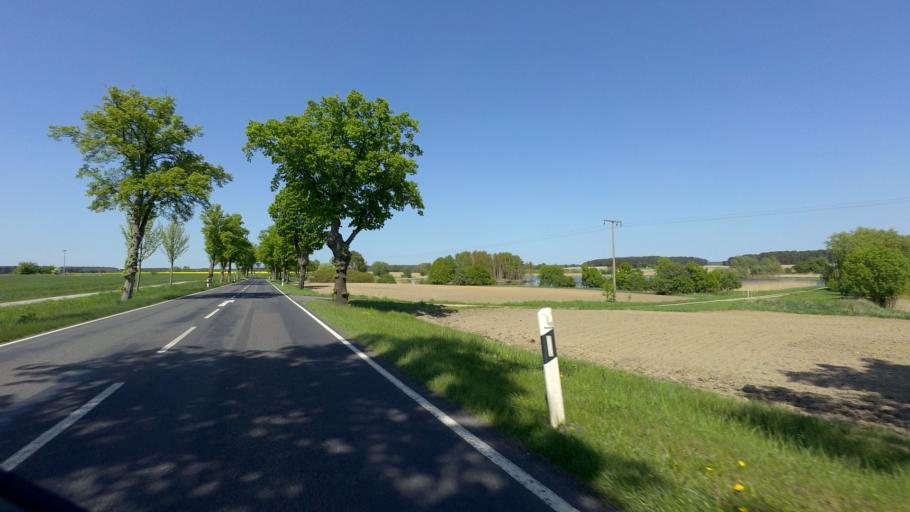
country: DE
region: Brandenburg
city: Friedland
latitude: 52.1192
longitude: 14.2566
